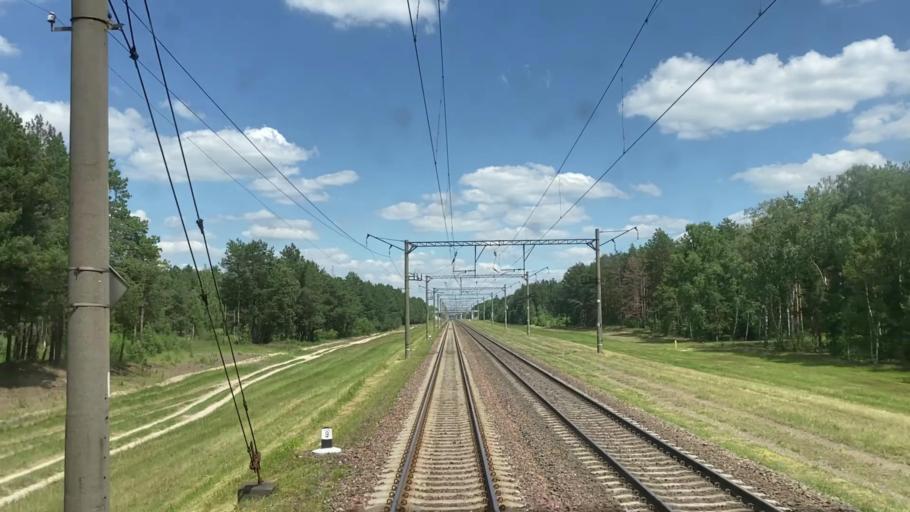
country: BY
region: Brest
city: Charnawchytsy
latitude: 52.1266
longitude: 23.7958
